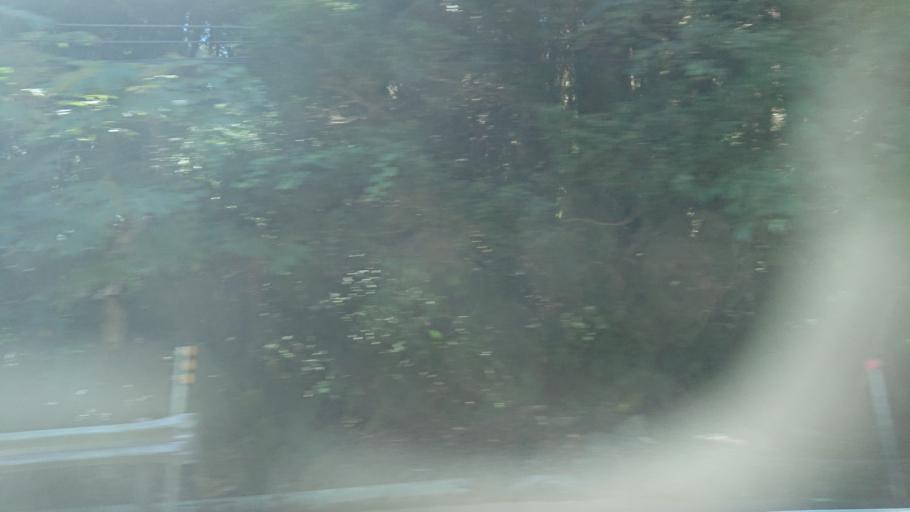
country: TW
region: Taiwan
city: Lugu
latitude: 23.4955
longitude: 120.7790
